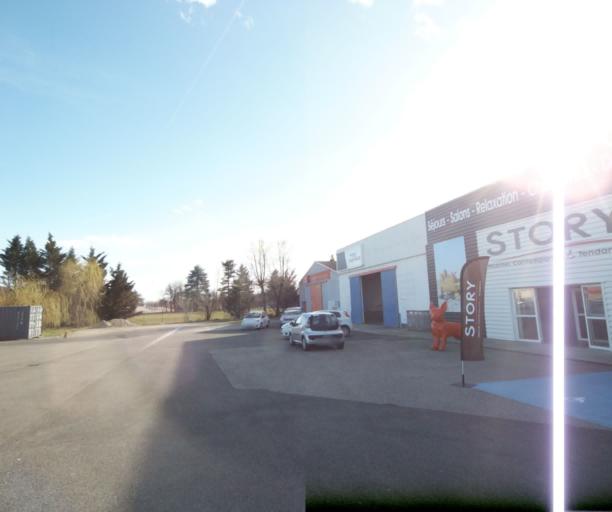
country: FR
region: Rhone-Alpes
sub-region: Departement de l'Ardeche
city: Davezieux
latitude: 45.2553
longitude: 4.6974
